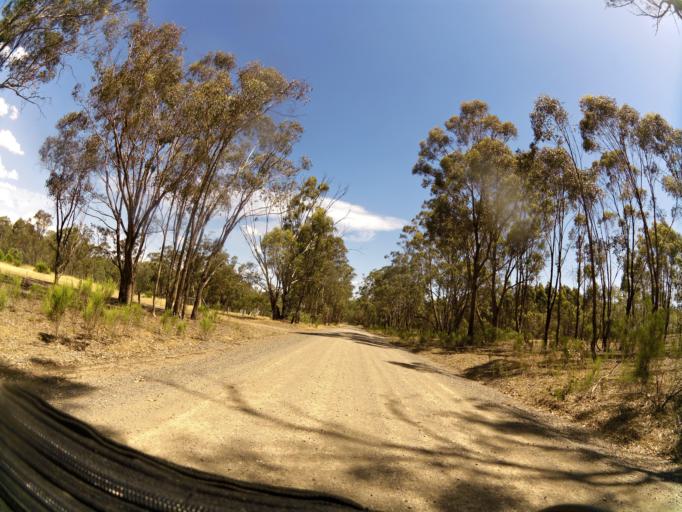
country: AU
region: Victoria
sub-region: Campaspe
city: Kyabram
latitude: -36.8214
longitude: 145.0795
